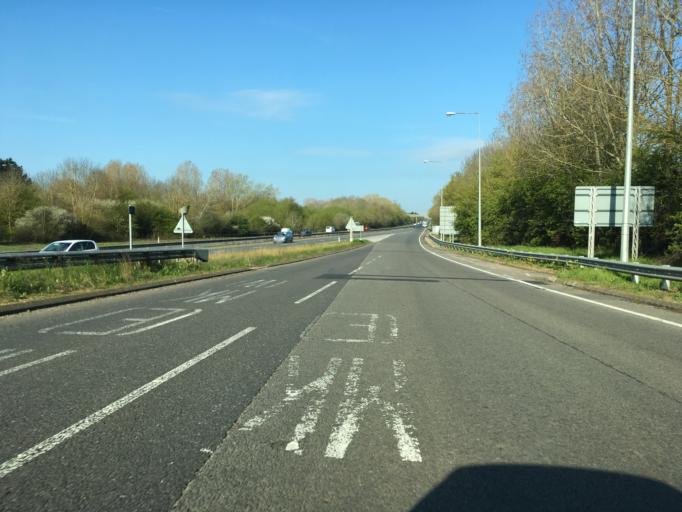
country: GB
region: England
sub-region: Milton Keynes
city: Bradwell
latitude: 52.0481
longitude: -0.8074
